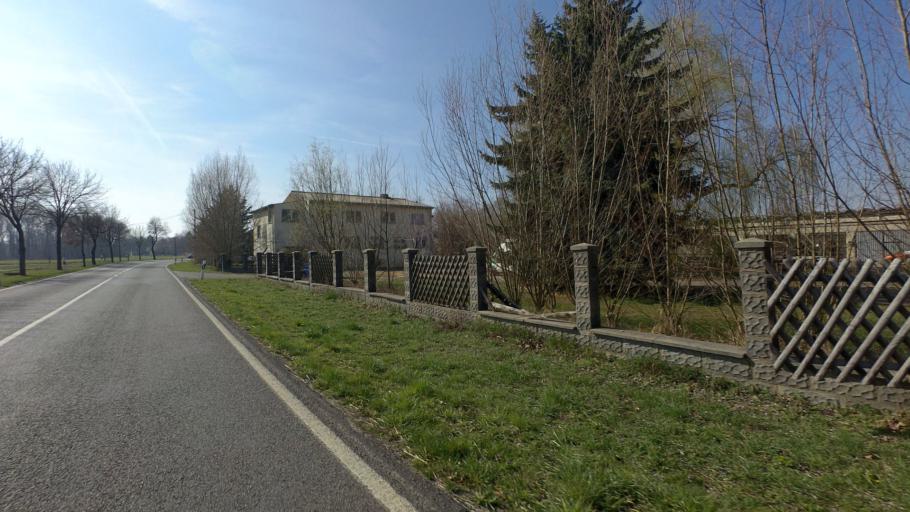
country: DE
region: Brandenburg
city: Sperenberg
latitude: 52.0544
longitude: 13.3235
